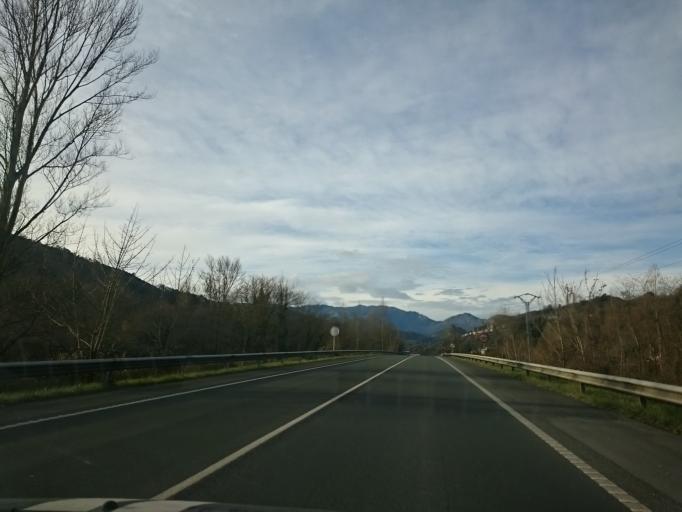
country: ES
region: Asturias
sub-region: Province of Asturias
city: Oviedo
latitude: 43.3170
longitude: -5.8121
